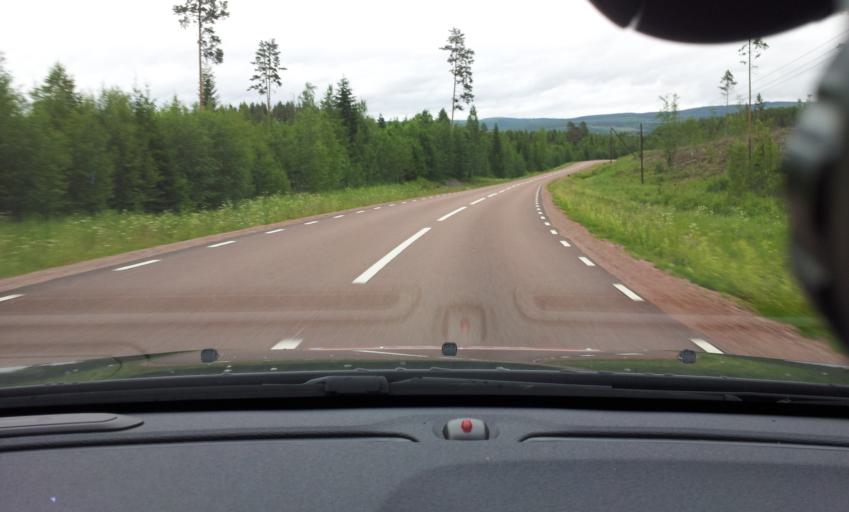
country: SE
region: Jaemtland
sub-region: Ragunda Kommun
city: Hammarstrand
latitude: 63.0201
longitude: 16.5879
